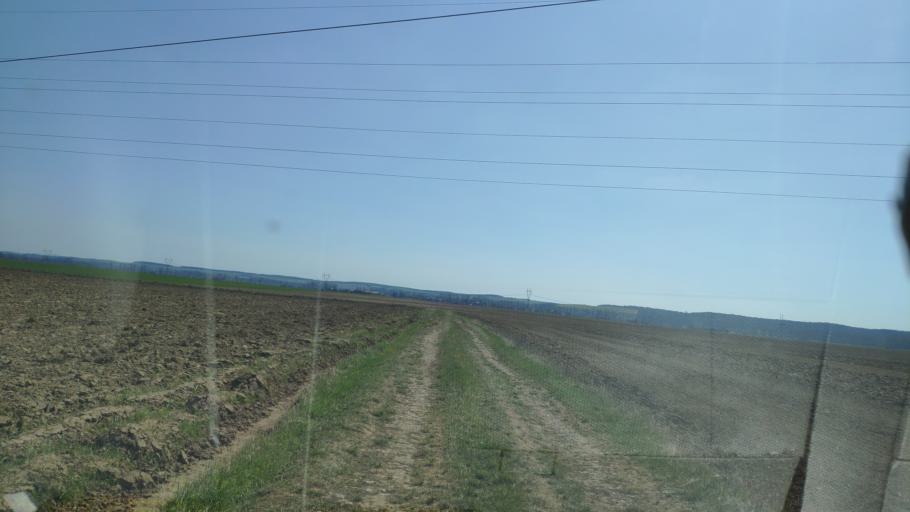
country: SK
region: Kosicky
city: Moldava nad Bodvou
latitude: 48.5986
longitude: 20.9456
